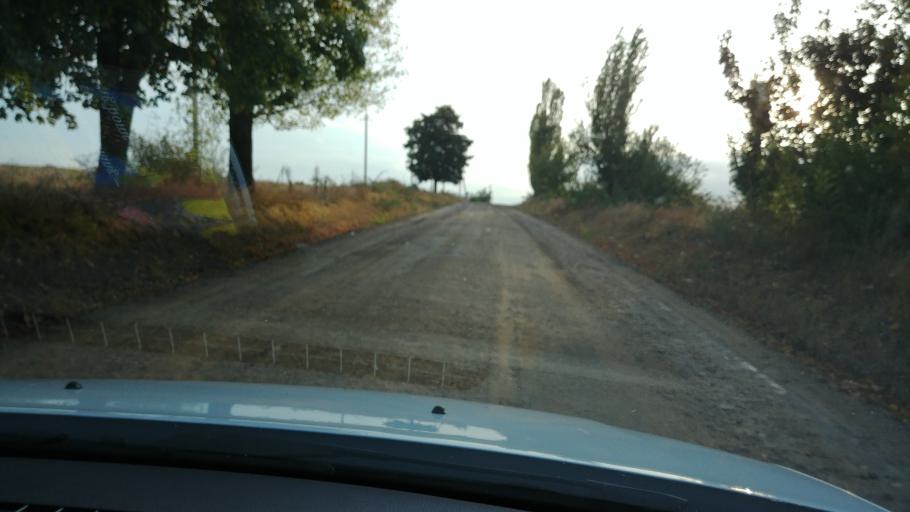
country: MD
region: Rezina
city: Saharna
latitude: 47.6788
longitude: 28.9667
